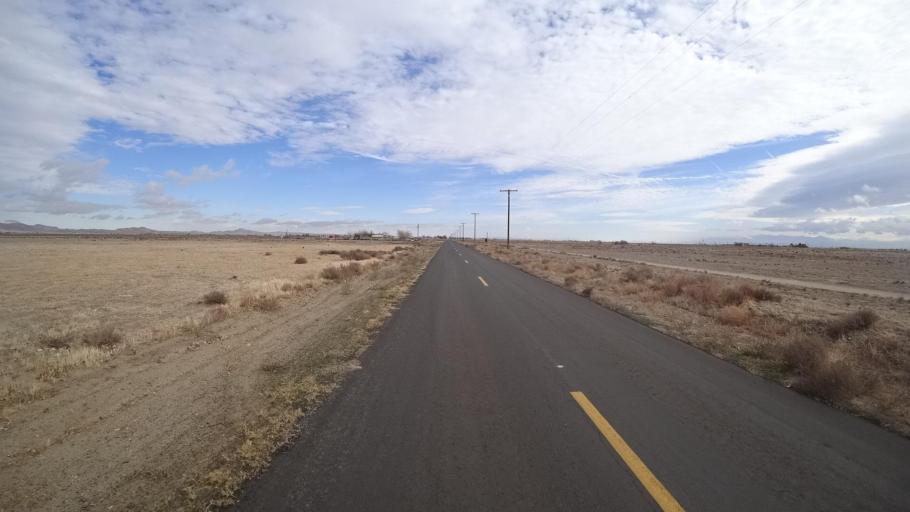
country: US
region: California
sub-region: Kern County
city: Rosamond
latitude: 34.8201
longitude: -118.3062
